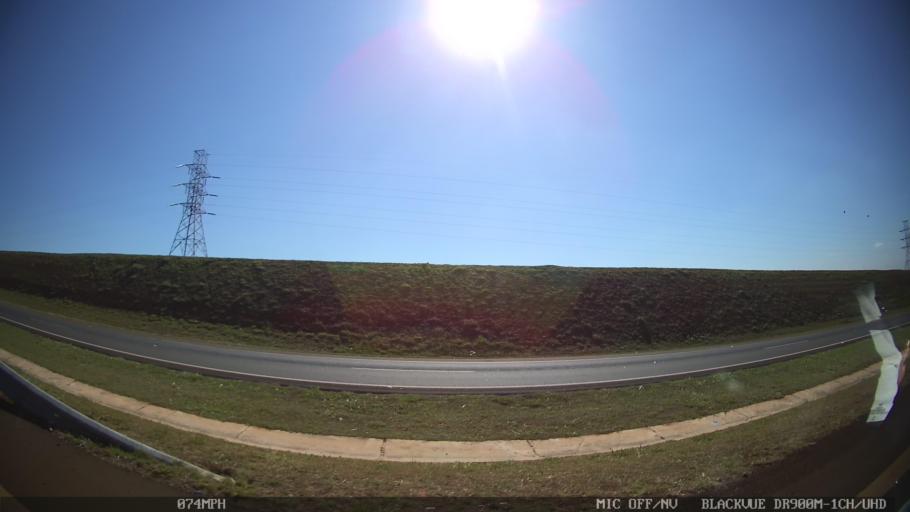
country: BR
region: Sao Paulo
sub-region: Ribeirao Preto
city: Ribeirao Preto
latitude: -21.1430
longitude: -47.8722
